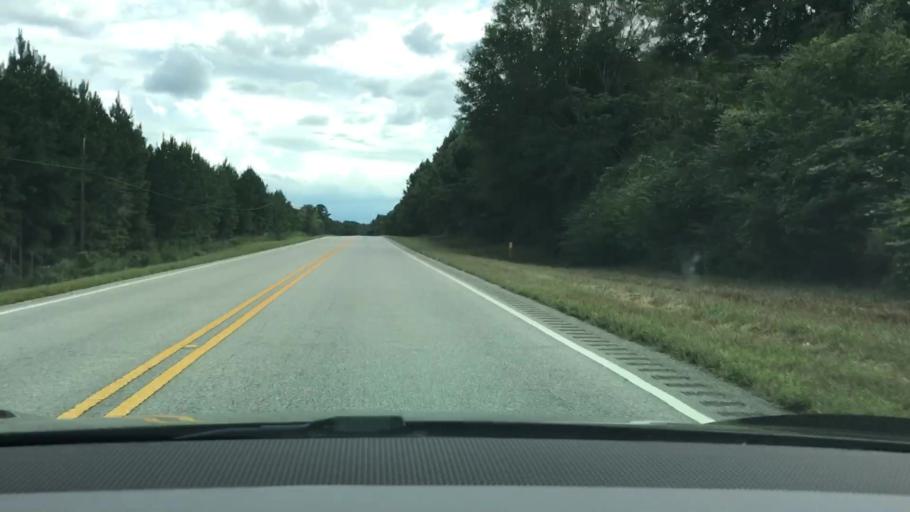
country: US
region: Alabama
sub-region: Pike County
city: Troy
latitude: 31.6304
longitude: -85.9748
